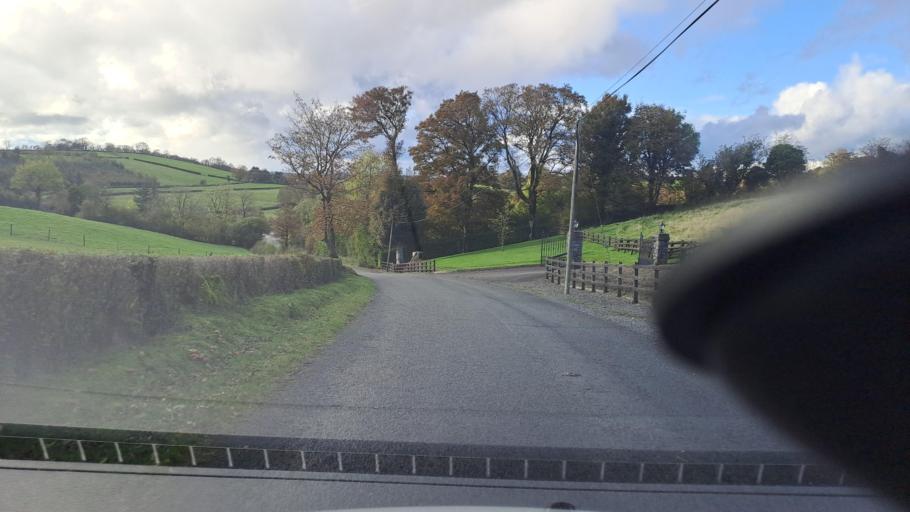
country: IE
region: Ulster
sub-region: An Cabhan
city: Bailieborough
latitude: 53.9387
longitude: -6.9597
